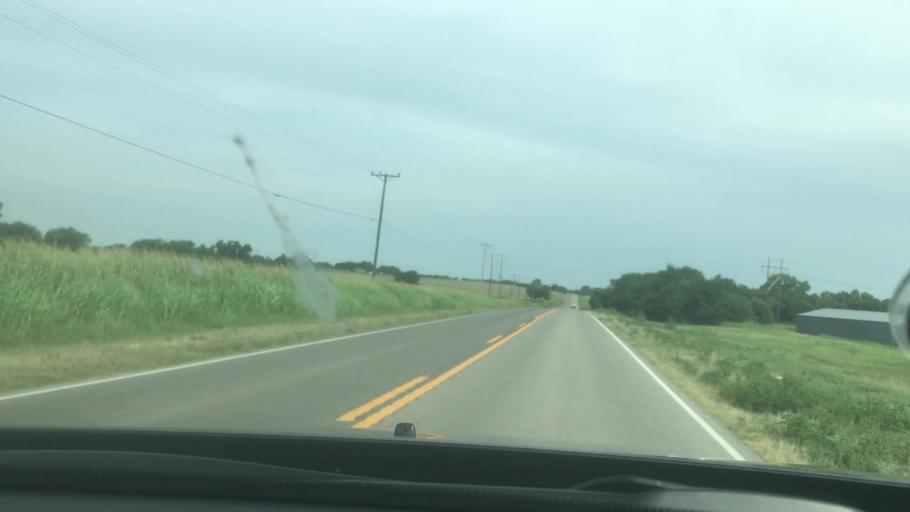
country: US
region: Oklahoma
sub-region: Garvin County
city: Maysville
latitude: 34.8032
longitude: -97.3662
